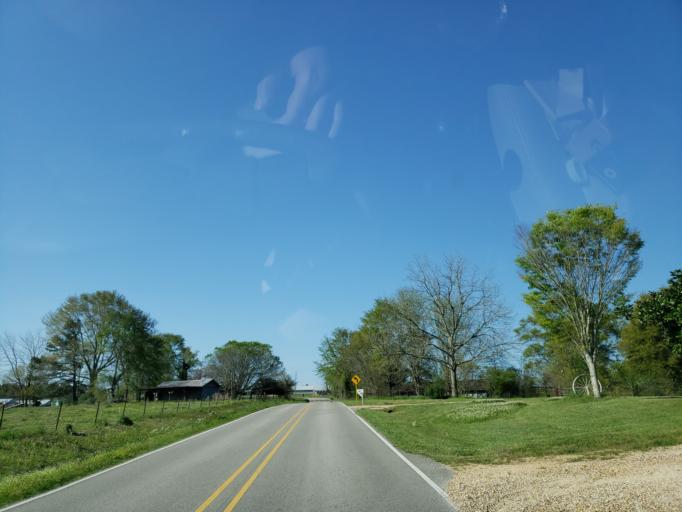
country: US
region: Mississippi
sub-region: Forrest County
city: Rawls Springs
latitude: 31.5549
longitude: -89.3658
